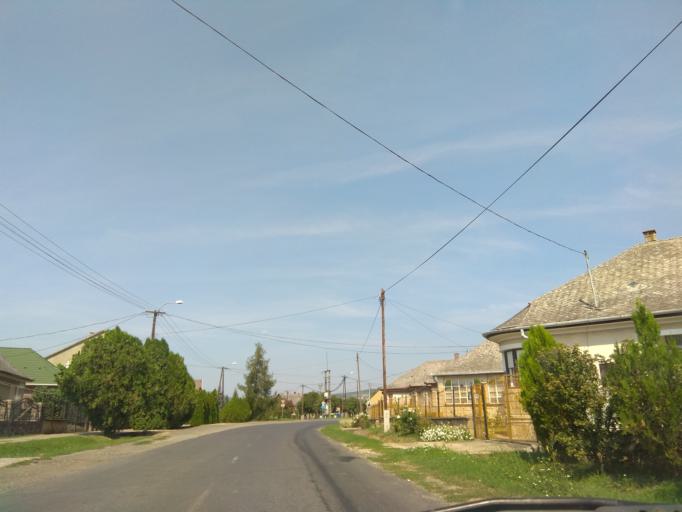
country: HU
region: Borsod-Abauj-Zemplen
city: Tallya
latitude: 48.2182
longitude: 21.2252
